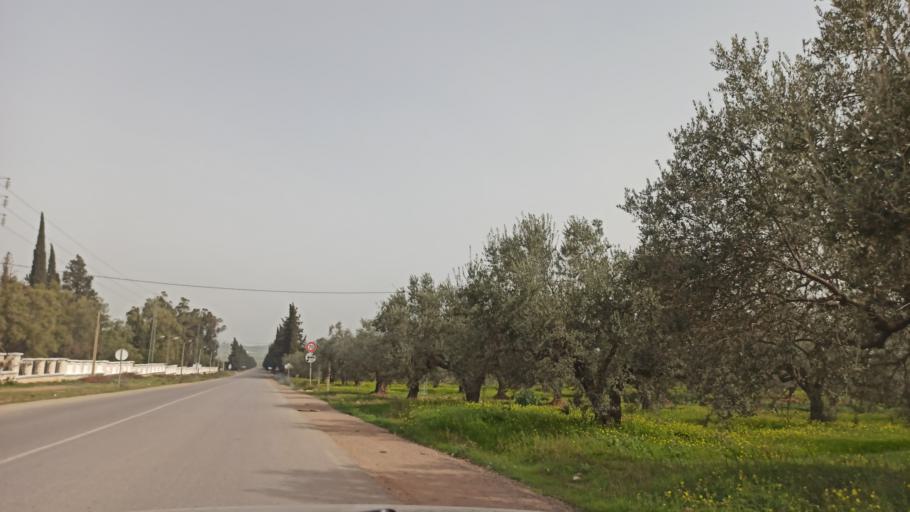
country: TN
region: Zaghwan
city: Zaghouan
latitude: 36.4264
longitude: 10.0953
